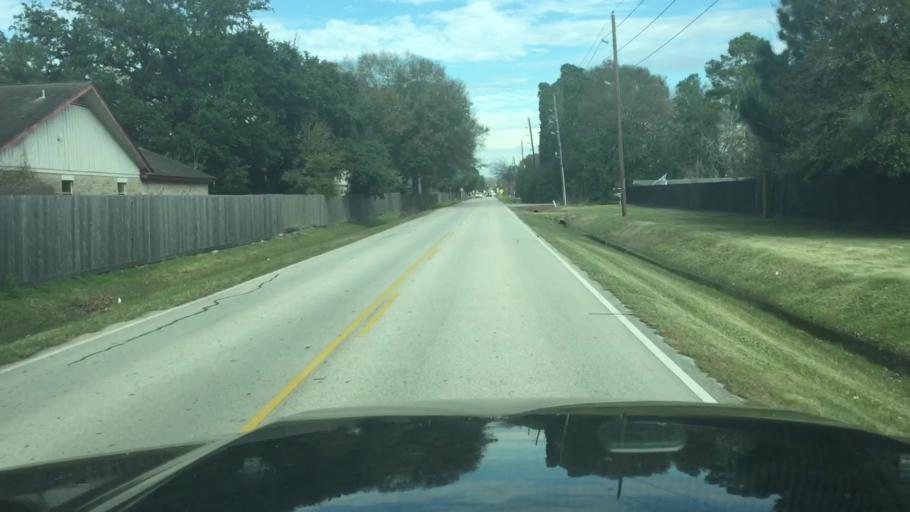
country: US
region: Texas
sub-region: Harris County
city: Oak Cliff Place
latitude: 29.8435
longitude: -95.6752
